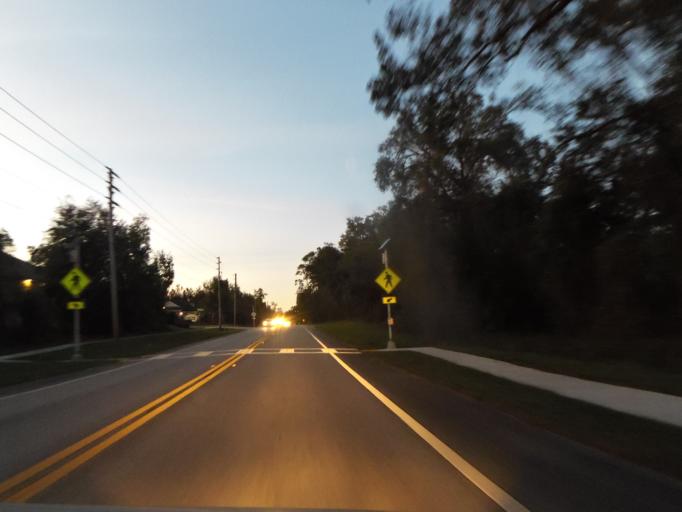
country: US
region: Florida
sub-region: Saint Johns County
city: Saint Augustine South
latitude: 29.8228
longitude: -81.3479
